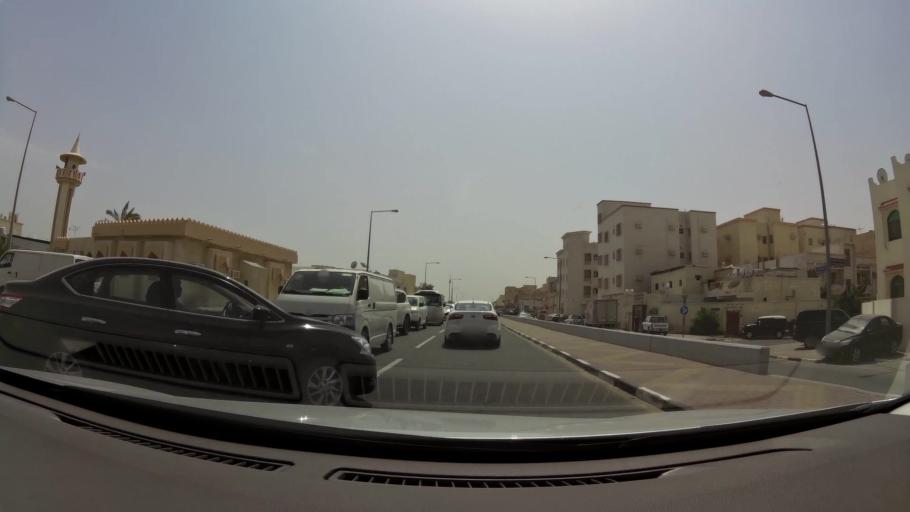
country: QA
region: Baladiyat ar Rayyan
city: Ar Rayyan
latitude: 25.3204
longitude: 51.4768
